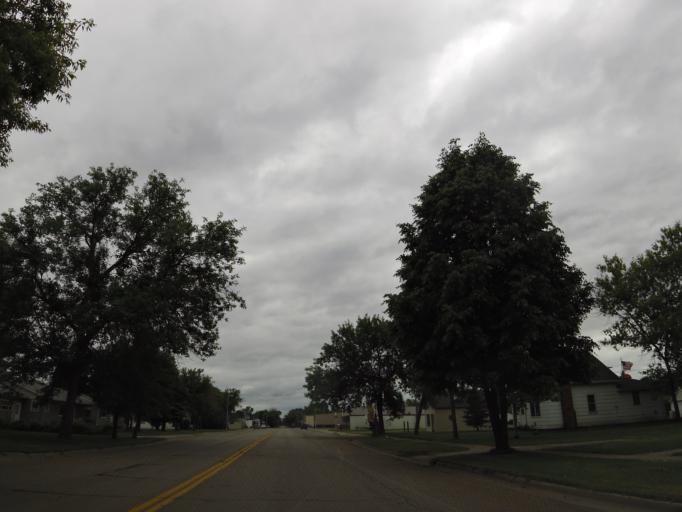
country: US
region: North Dakota
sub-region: Walsh County
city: Grafton
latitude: 48.6211
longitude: -97.4490
